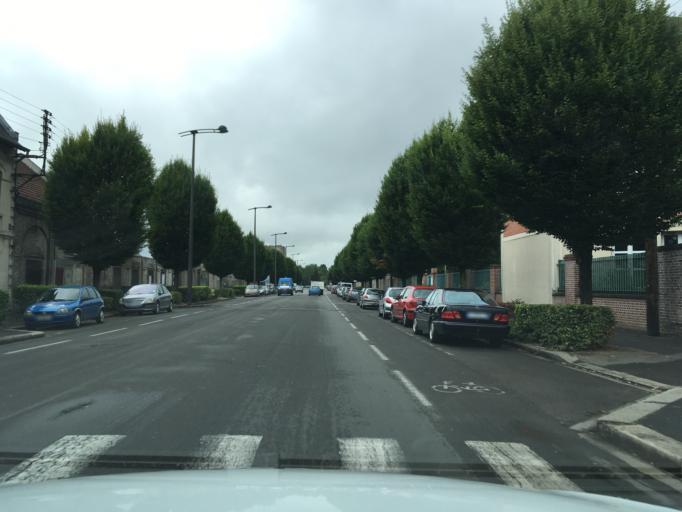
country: FR
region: Picardie
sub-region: Departement de l'Aisne
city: Saint-Quentin
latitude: 49.8423
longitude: 3.2831
